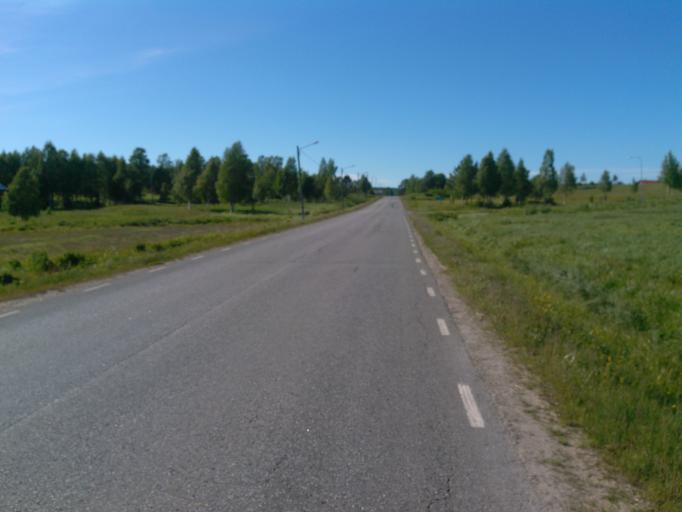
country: SE
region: Vaesterbotten
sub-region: Umea Kommun
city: Roback
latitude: 63.8248
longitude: 20.1239
